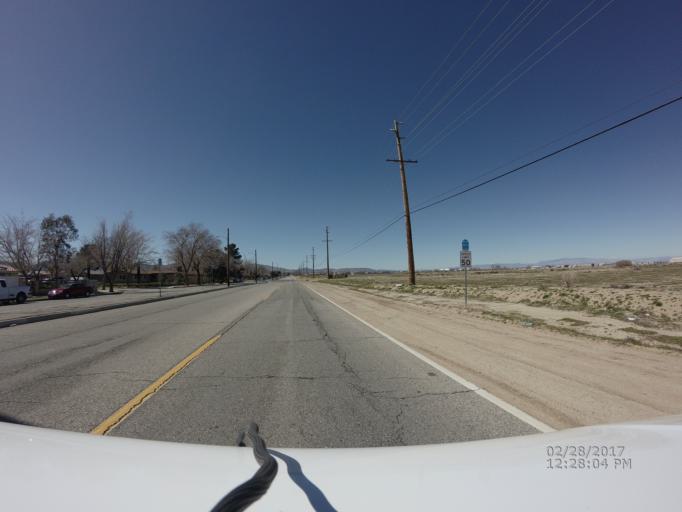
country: US
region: California
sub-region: Los Angeles County
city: Palmdale
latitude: 34.5875
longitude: -118.0659
